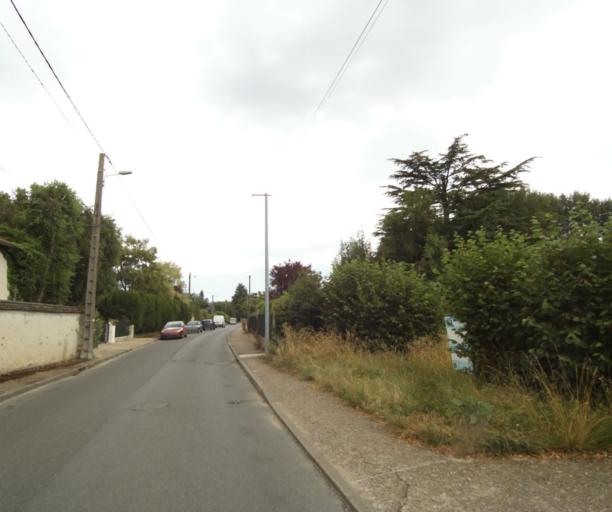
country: FR
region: Ile-de-France
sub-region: Departement de Seine-et-Marne
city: Perthes
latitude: 48.4795
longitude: 2.5503
